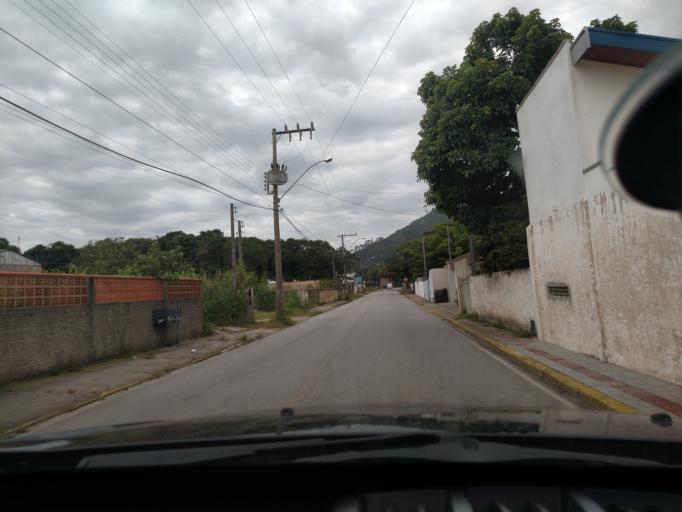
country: BR
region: Santa Catarina
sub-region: Porto Belo
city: Porto Belo
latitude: -27.1941
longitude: -48.5023
